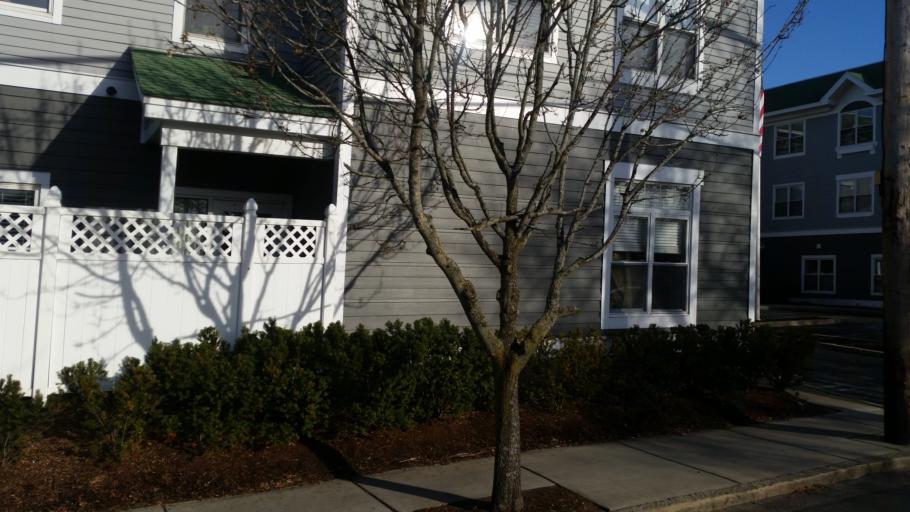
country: US
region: Massachusetts
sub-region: Middlesex County
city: Cambridge
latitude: 42.3875
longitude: -71.1319
